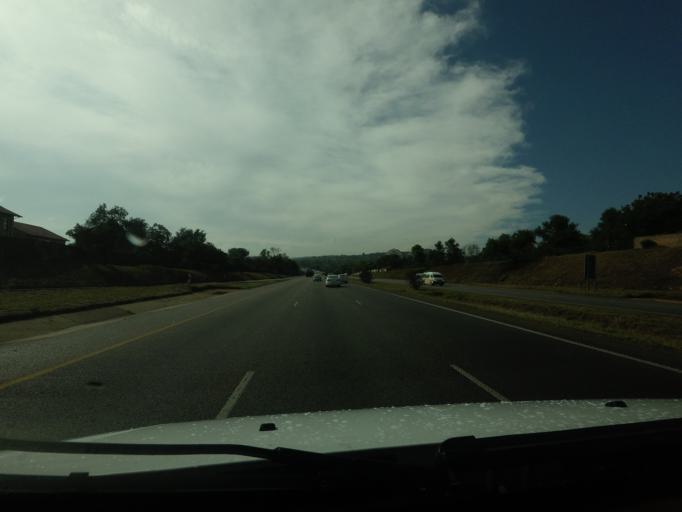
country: ZA
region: Gauteng
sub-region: City of Tshwane Metropolitan Municipality
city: Pretoria
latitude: -25.7474
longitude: 28.2938
